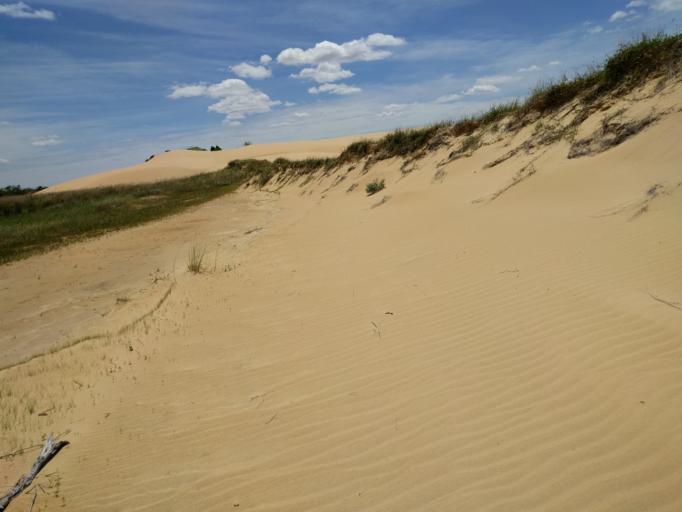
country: BO
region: Santa Cruz
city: Santa Cruz de la Sierra
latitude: -17.9545
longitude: -63.1518
